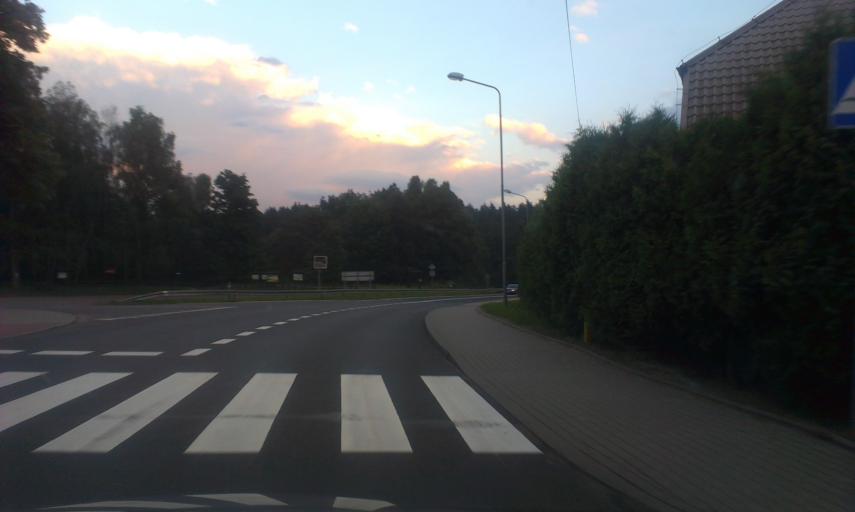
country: PL
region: West Pomeranian Voivodeship
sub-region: Powiat koszalinski
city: Sianow
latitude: 54.0765
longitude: 16.3948
